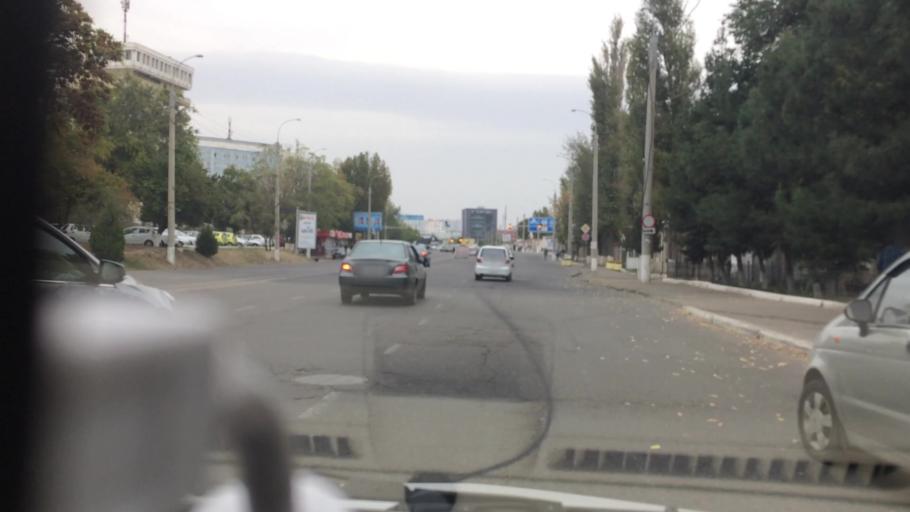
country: UZ
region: Toshkent
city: Salor
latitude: 41.3179
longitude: 69.3142
